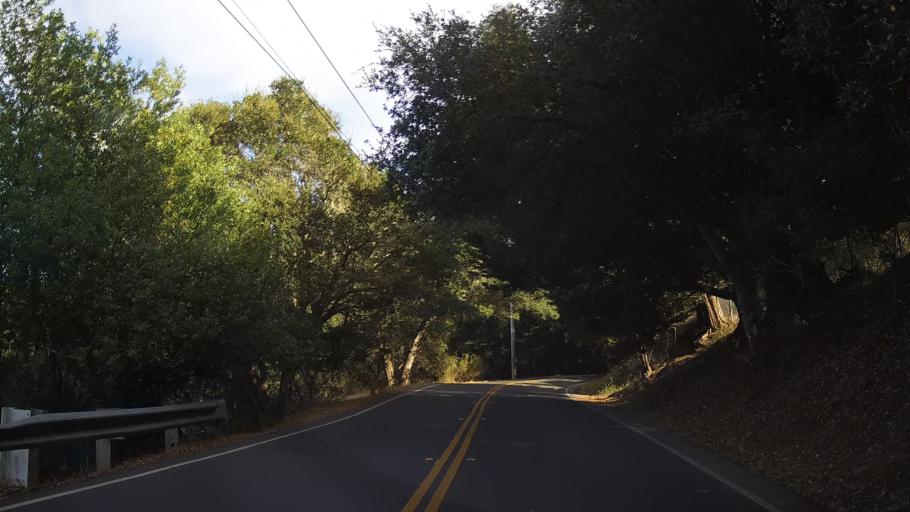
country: US
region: California
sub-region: Contra Costa County
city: Kensington
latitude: 37.9035
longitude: -122.2638
